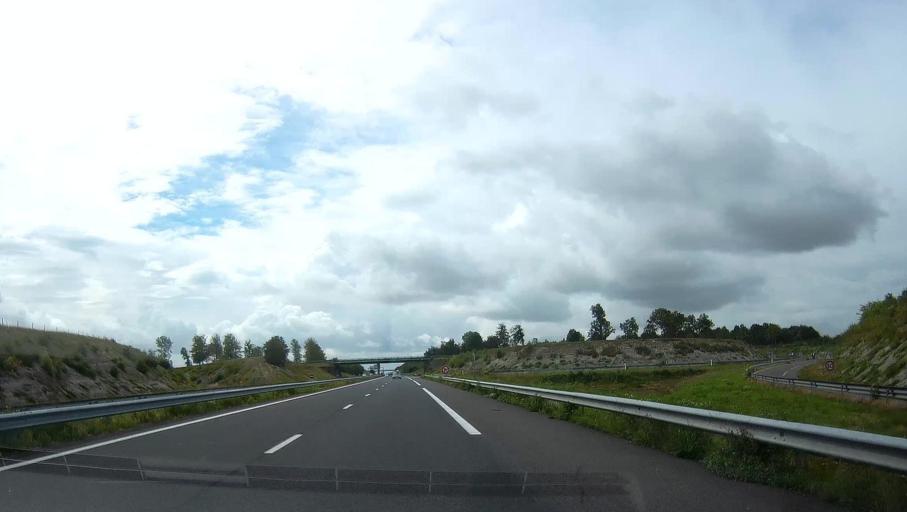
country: FR
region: Champagne-Ardenne
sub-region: Departement de la Marne
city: Fagnieres
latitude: 48.9088
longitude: 4.2839
